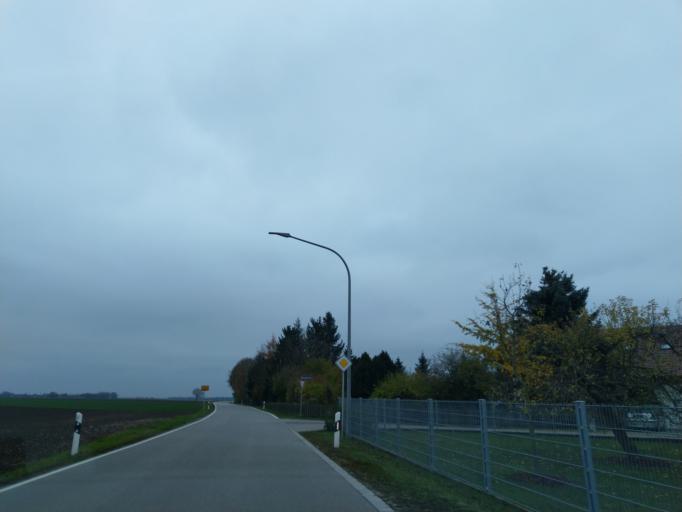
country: DE
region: Bavaria
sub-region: Lower Bavaria
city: Wallersdorf
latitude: 48.7809
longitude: 12.7553
